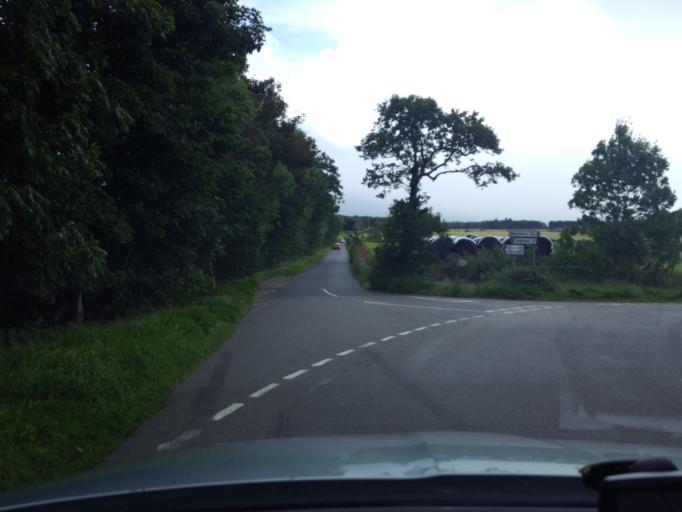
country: GB
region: Scotland
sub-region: Aberdeenshire
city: Banchory
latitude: 57.0871
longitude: -2.4483
